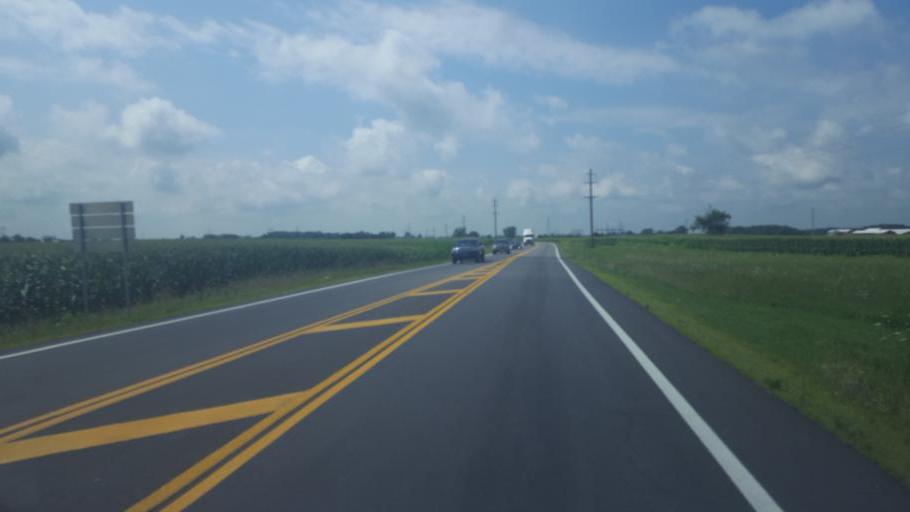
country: US
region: Ohio
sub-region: Fairfield County
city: Millersport
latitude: 39.8984
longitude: -82.5633
